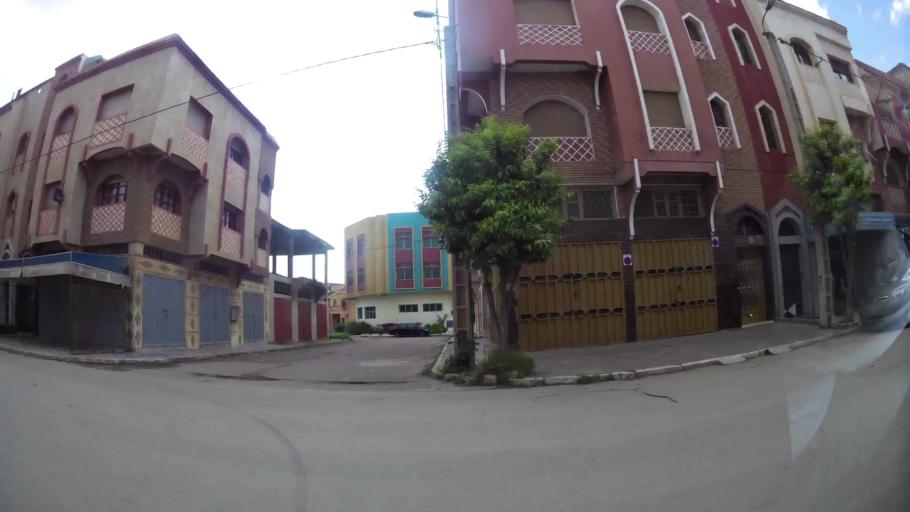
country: MA
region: Grand Casablanca
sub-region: Mediouna
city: Mediouna
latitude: 33.3753
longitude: -7.5347
